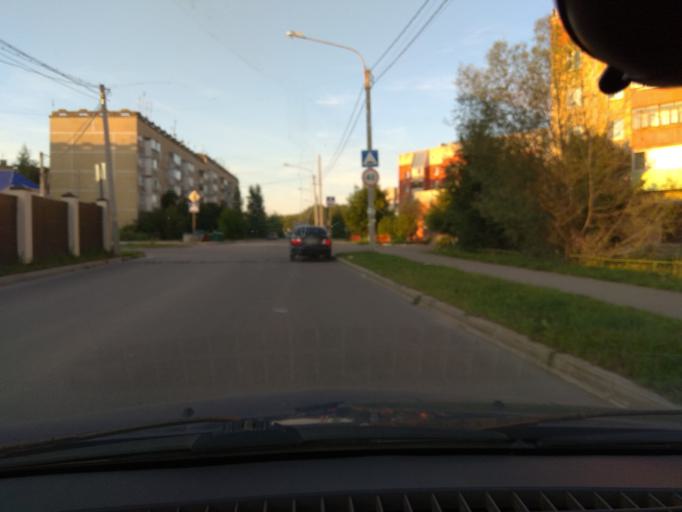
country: RU
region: Kaluga
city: Mstikhino
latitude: 54.5614
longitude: 36.1332
